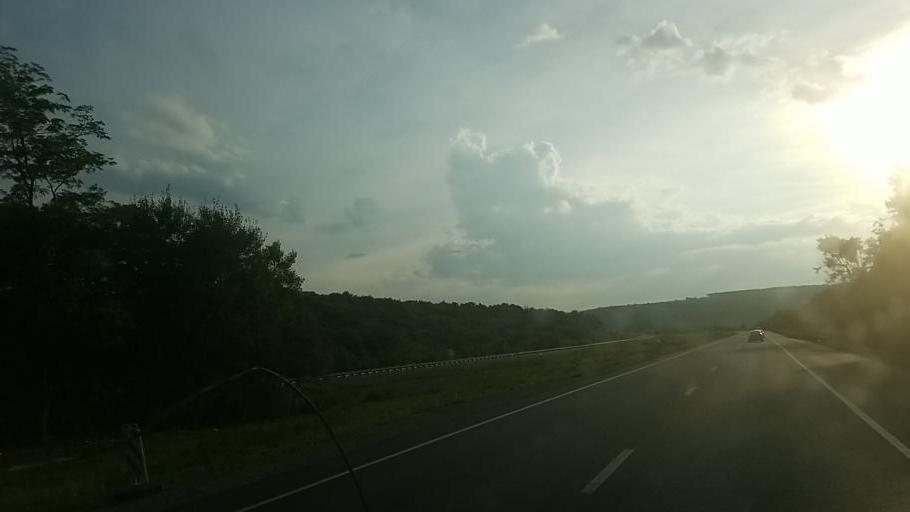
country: US
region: Pennsylvania
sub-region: Clearfield County
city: Troy
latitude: 40.9703
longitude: -78.0709
